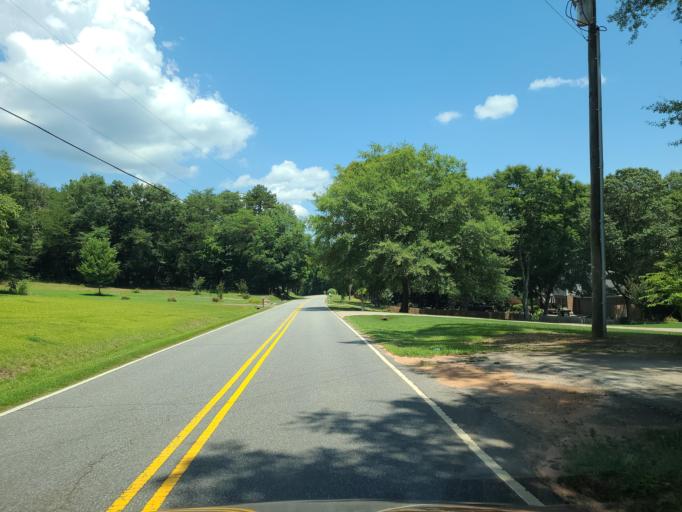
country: US
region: South Carolina
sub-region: Spartanburg County
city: Inman Mills
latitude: 35.0335
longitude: -82.1778
